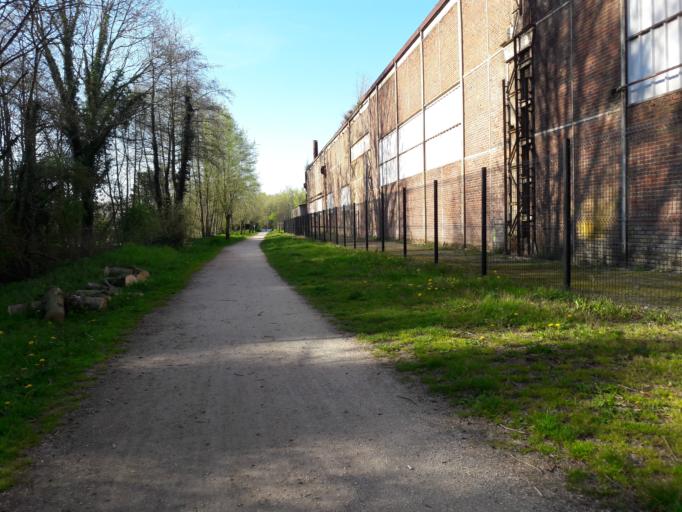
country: FR
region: Nord-Pas-de-Calais
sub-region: Departement du Nord
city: Ferriere-la-Grande
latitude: 50.2512
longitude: 4.0055
